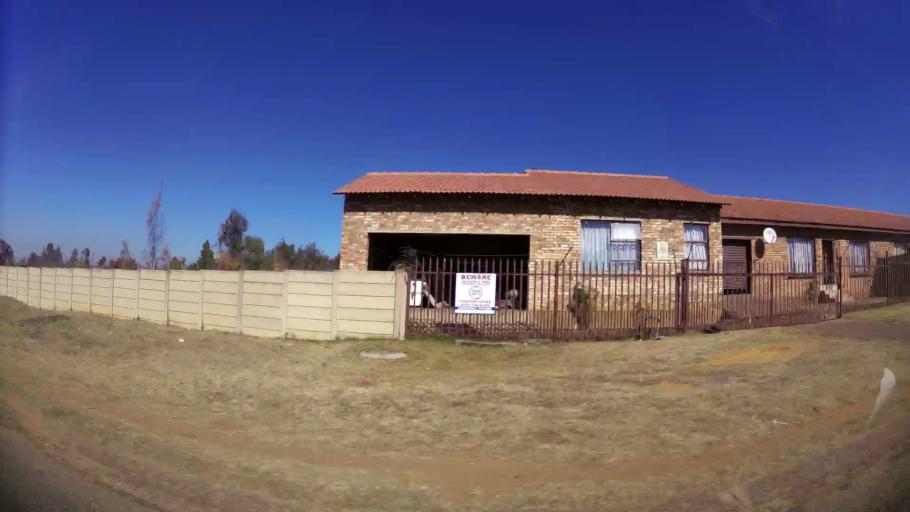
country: ZA
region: Mpumalanga
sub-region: Nkangala District Municipality
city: Witbank
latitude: -25.8344
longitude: 29.2443
